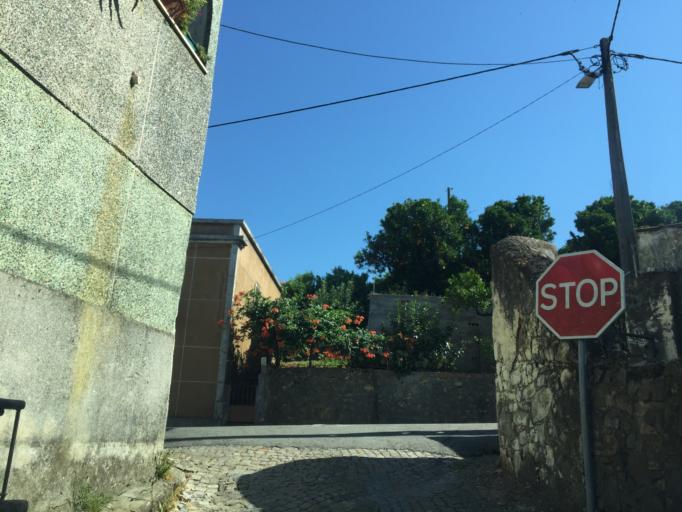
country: PT
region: Santarem
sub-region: Ferreira do Zezere
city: Ferreira do Zezere
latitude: 39.5999
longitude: -8.3030
